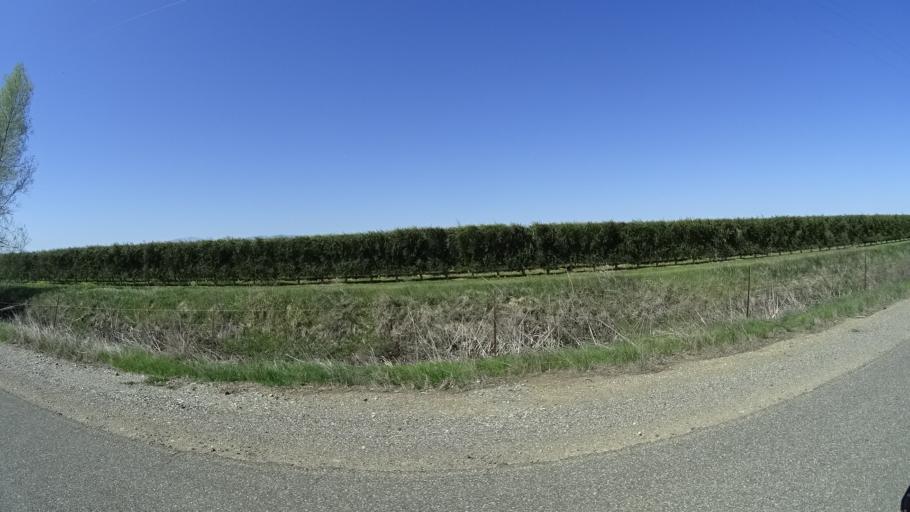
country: US
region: California
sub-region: Glenn County
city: Orland
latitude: 39.6469
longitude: -122.2533
